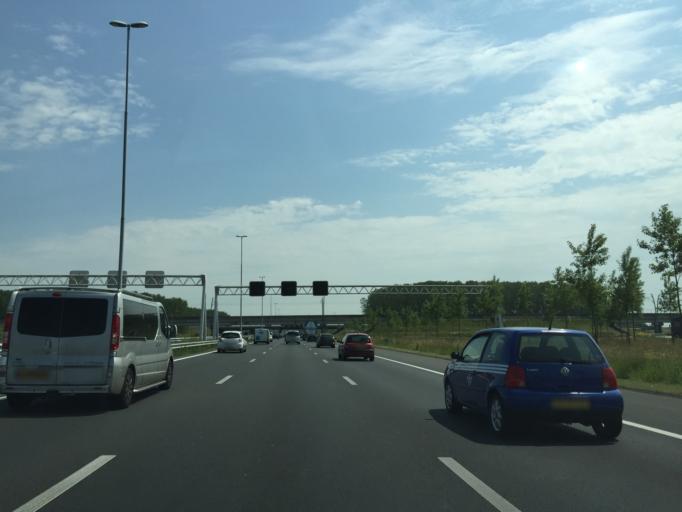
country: NL
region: Gelderland
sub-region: Gemeente Zaltbommel
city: Zaltbommel
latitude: 51.8606
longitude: 5.2252
